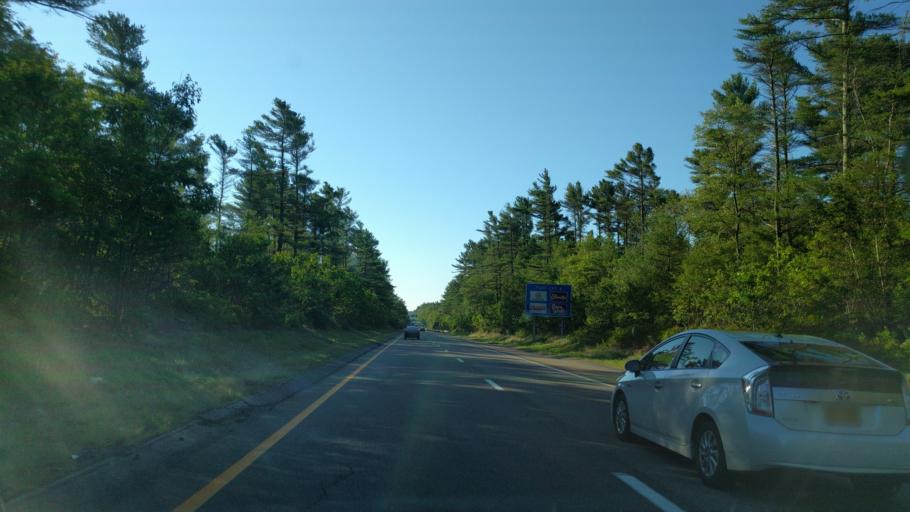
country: US
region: Massachusetts
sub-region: Plymouth County
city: Middleborough Center
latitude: 41.9140
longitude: -70.9825
